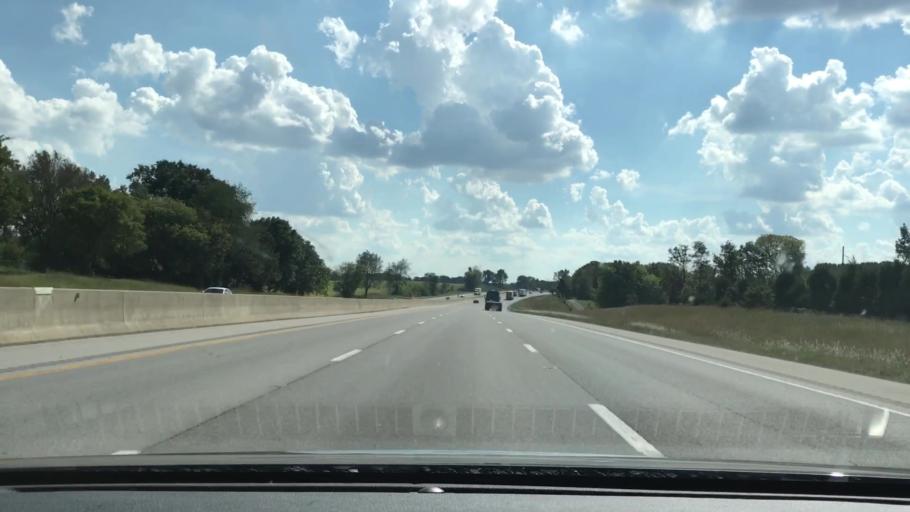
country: US
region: Kentucky
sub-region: Warren County
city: Plano
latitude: 36.7919
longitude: -86.4752
